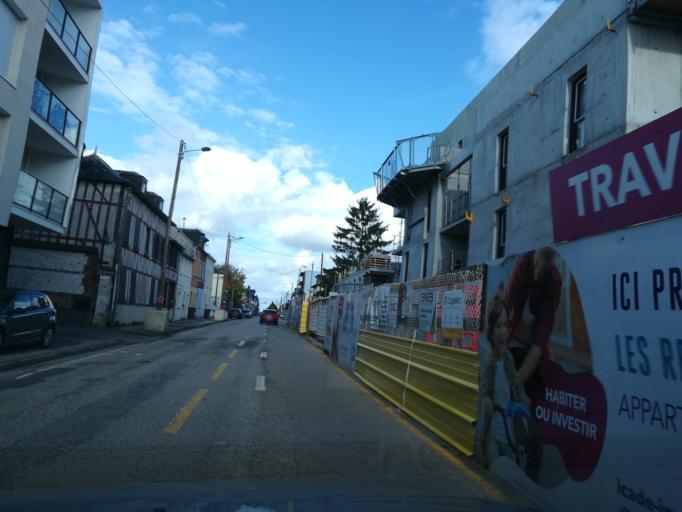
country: FR
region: Haute-Normandie
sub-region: Departement de la Seine-Maritime
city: Bois-Guillaume
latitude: 49.4717
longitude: 1.1220
